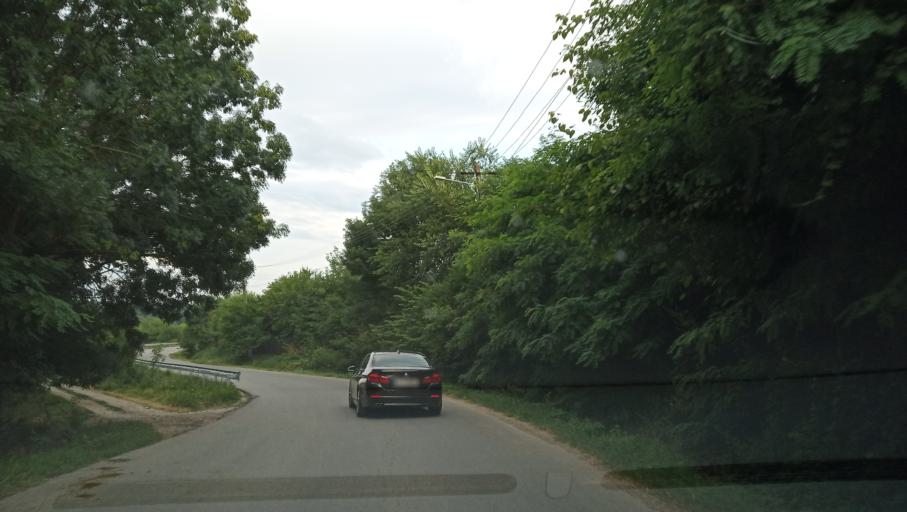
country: RO
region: Giurgiu
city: Iepuresti
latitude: 44.2565
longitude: 25.8905
